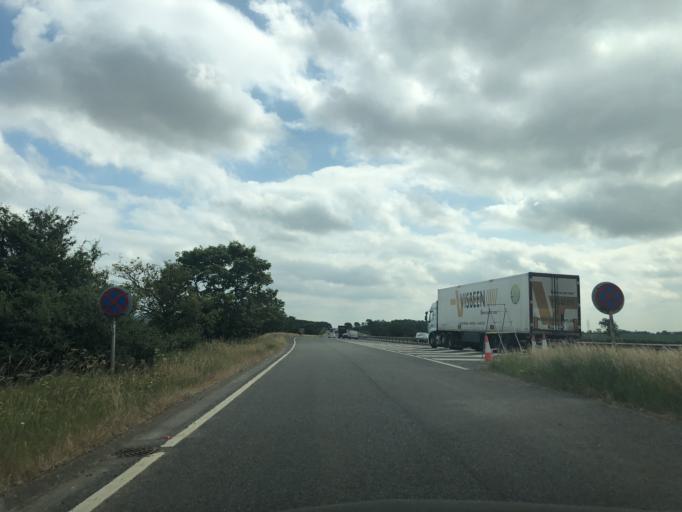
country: GB
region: England
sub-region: Stockton-on-Tees
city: Yarm
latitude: 54.4537
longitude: -1.3221
